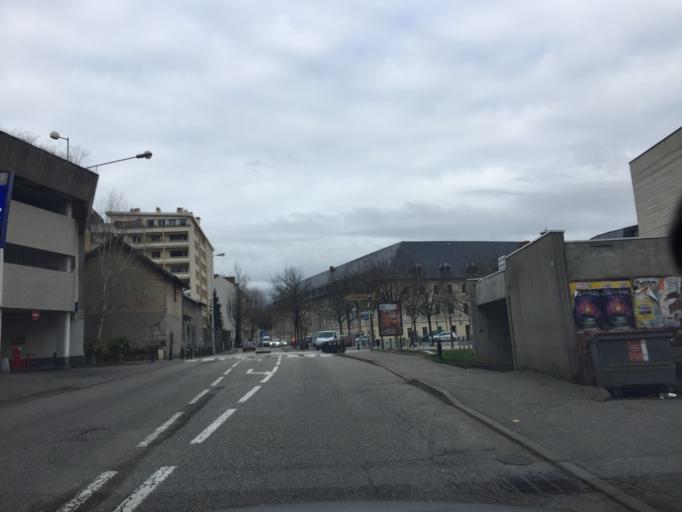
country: FR
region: Rhone-Alpes
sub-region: Departement de la Savoie
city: Chambery
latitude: 45.5624
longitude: 5.9265
